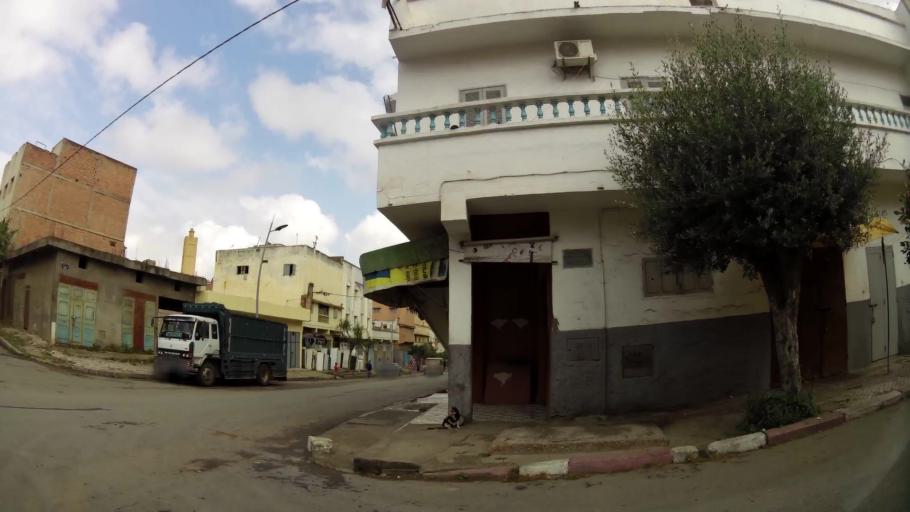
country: MA
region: Rabat-Sale-Zemmour-Zaer
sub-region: Khemisset
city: Tiflet
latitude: 33.8949
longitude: -6.3117
